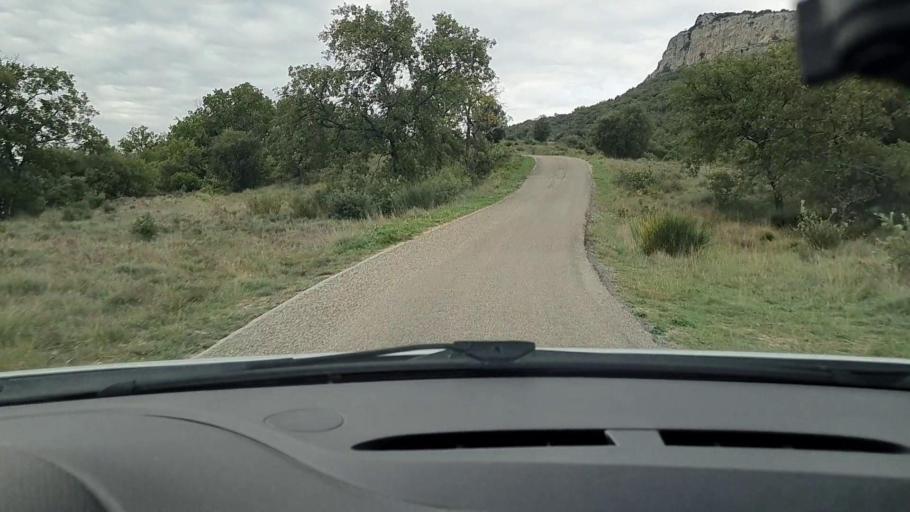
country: FR
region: Languedoc-Roussillon
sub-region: Departement du Gard
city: Mons
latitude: 44.1477
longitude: 4.2911
